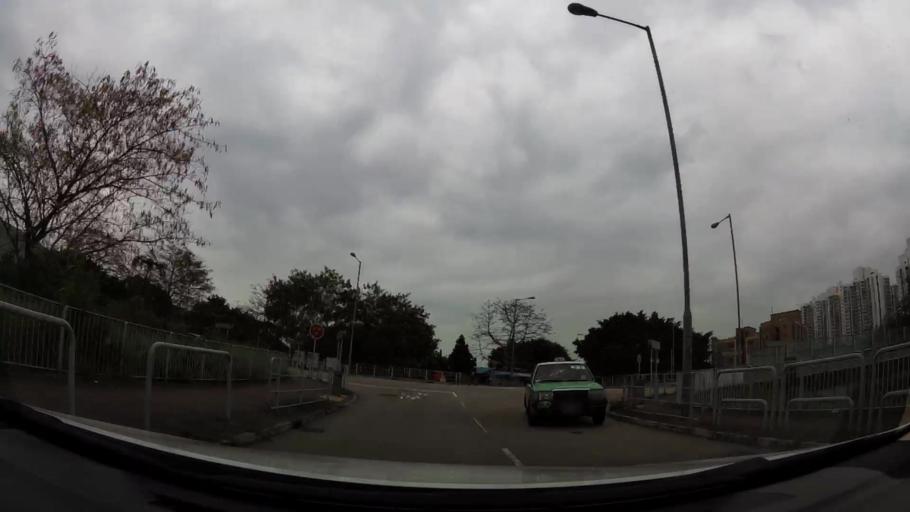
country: HK
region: Yuen Long
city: Yuen Long Kau Hui
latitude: 22.4346
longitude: 113.9953
